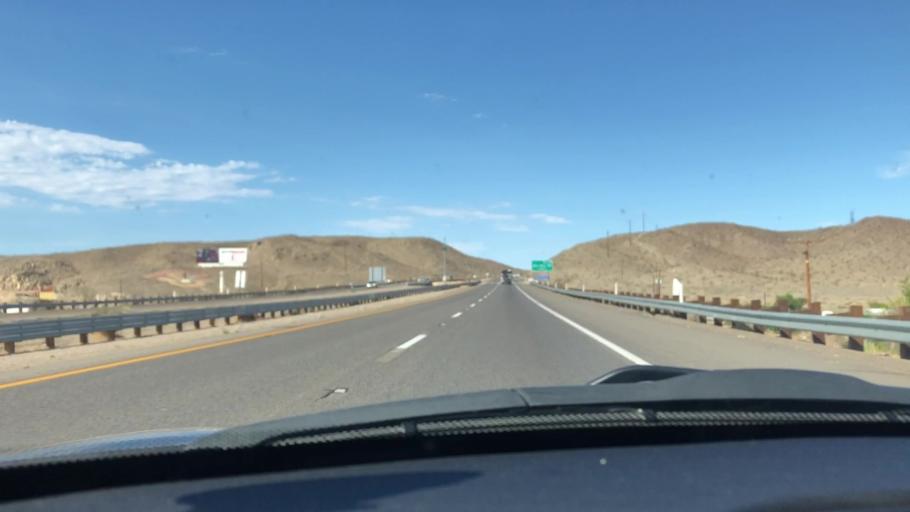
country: US
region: California
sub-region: San Bernardino County
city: Barstow
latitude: 34.9010
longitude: -116.9877
